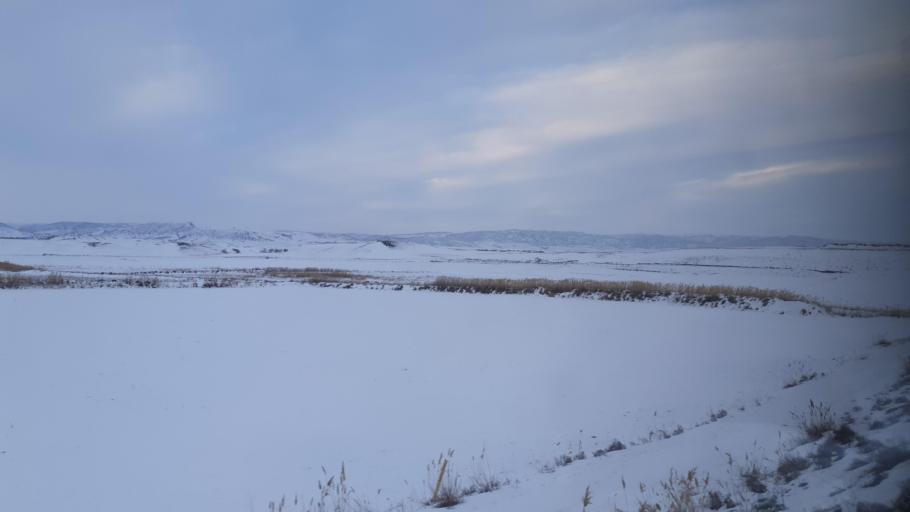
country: TR
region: Yozgat
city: Yerkoy
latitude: 39.6859
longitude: 34.4172
